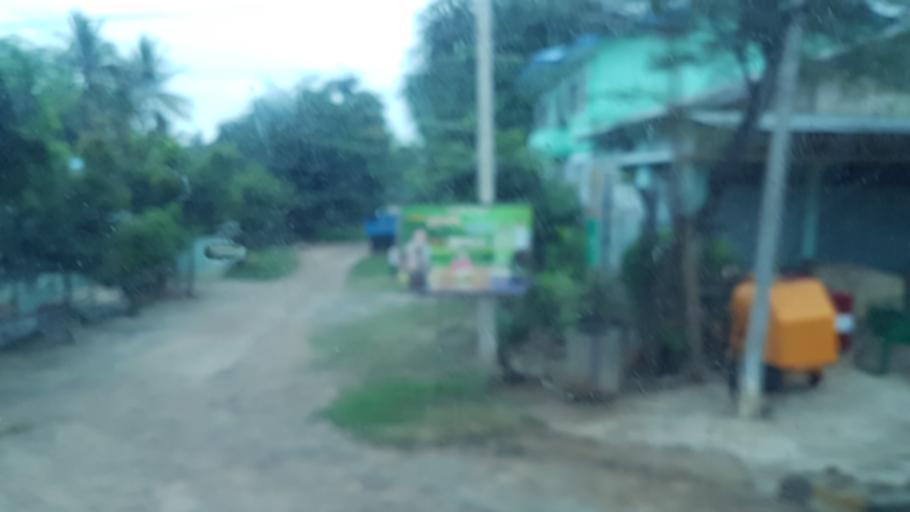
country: MM
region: Magway
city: Magway
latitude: 20.1540
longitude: 94.9401
